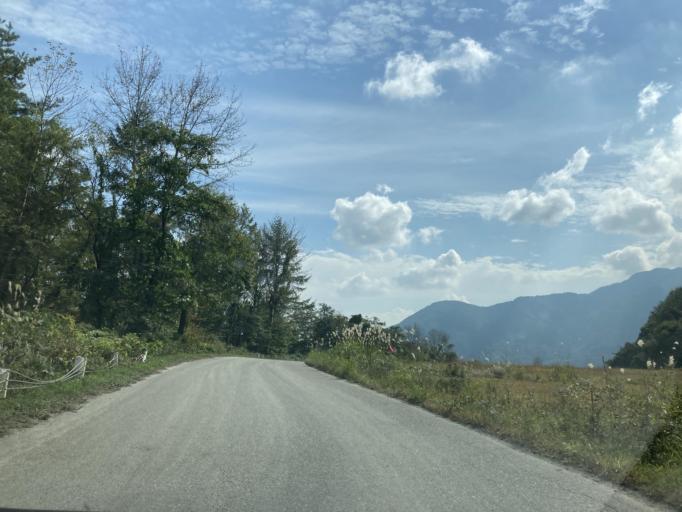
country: JP
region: Nagano
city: Omachi
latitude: 36.5310
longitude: 137.7885
